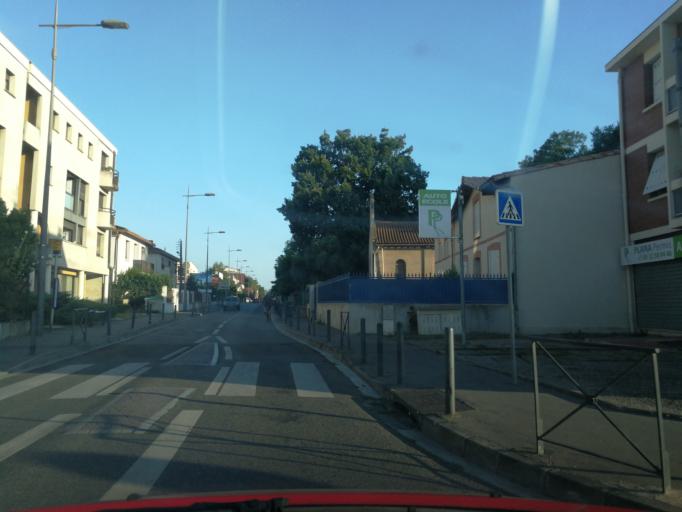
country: FR
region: Midi-Pyrenees
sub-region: Departement de la Haute-Garonne
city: Balma
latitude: 43.6139
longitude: 1.4761
